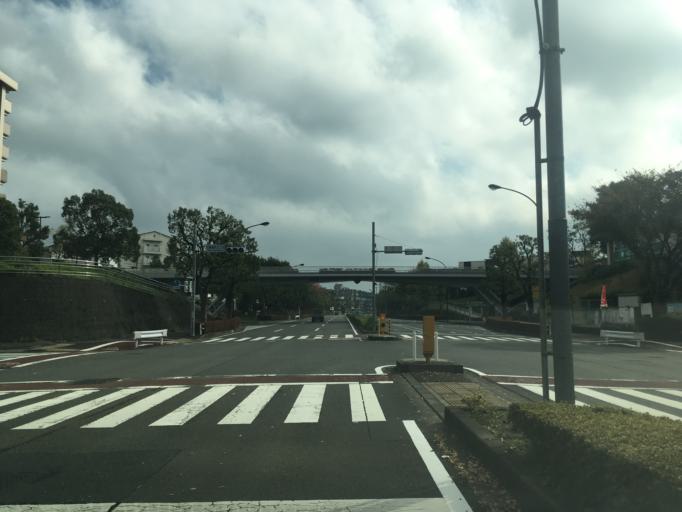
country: JP
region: Tokyo
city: Hino
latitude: 35.6126
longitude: 139.4236
